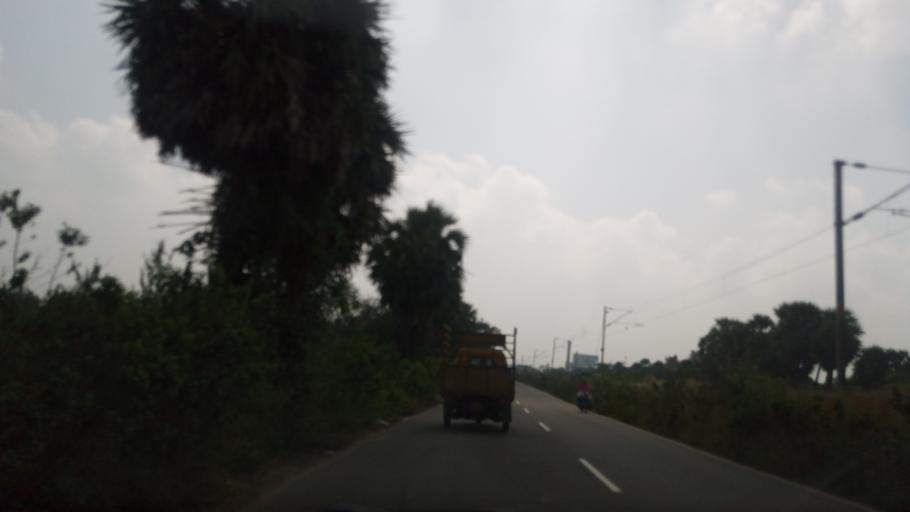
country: IN
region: Tamil Nadu
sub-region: Kancheepuram
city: Kanchipuram
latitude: 12.8823
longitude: 79.6887
